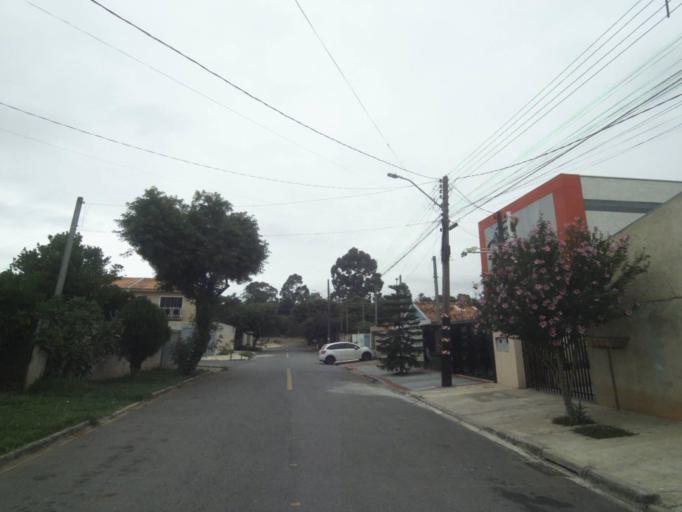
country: BR
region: Parana
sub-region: Araucaria
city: Araucaria
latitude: -25.5519
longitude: -49.3390
